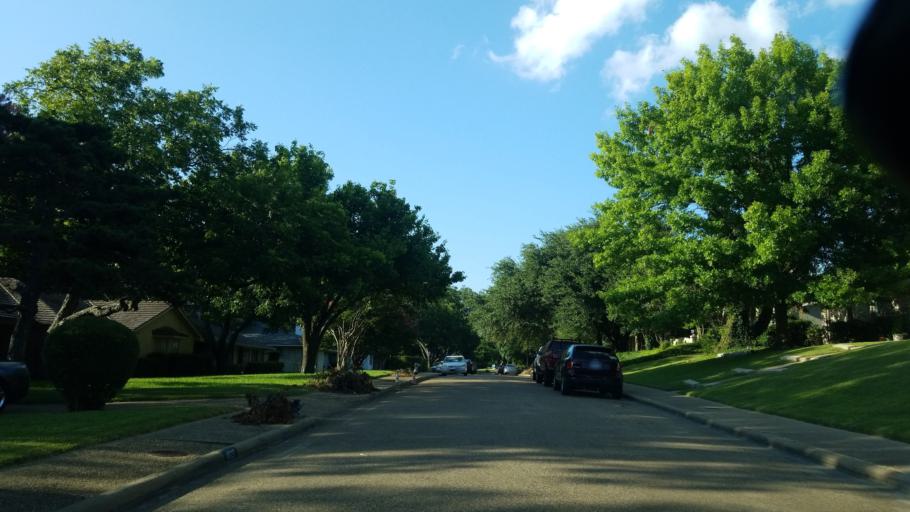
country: US
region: Texas
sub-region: Dallas County
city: Dallas
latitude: 32.7820
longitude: -96.7135
